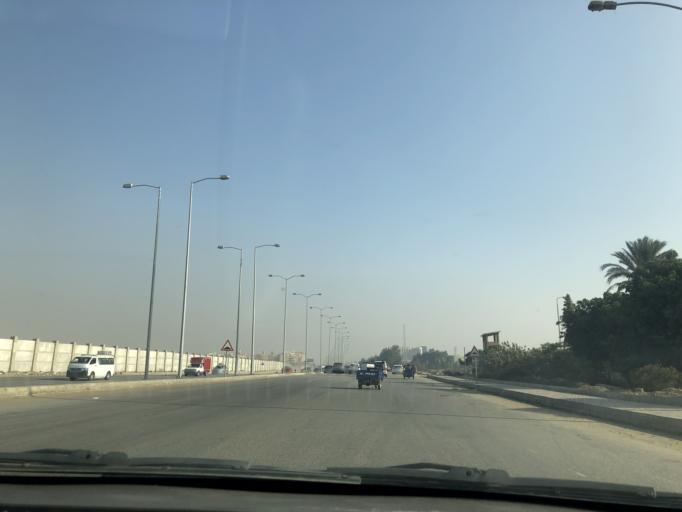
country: EG
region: Al Jizah
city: Madinat Sittah Uktubar
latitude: 29.9555
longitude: 31.0791
